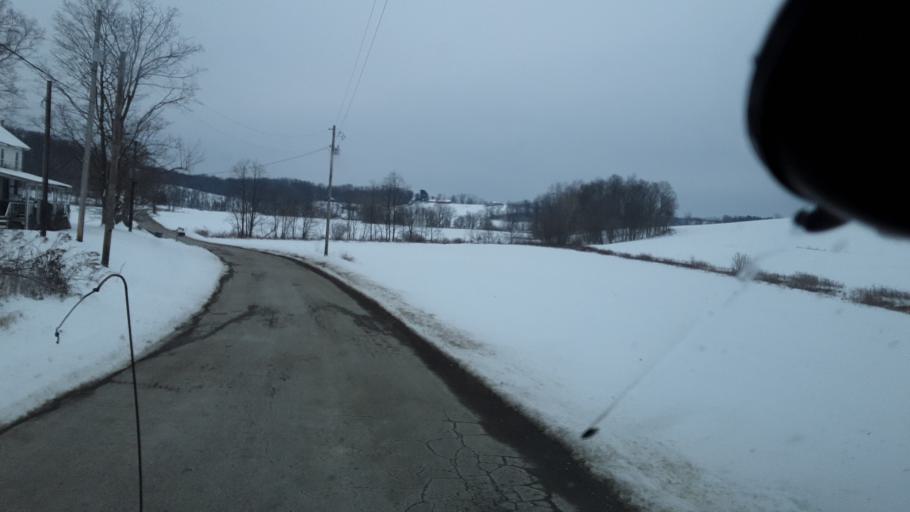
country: US
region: Ohio
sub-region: Perry County
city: Somerset
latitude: 39.9152
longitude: -82.1936
